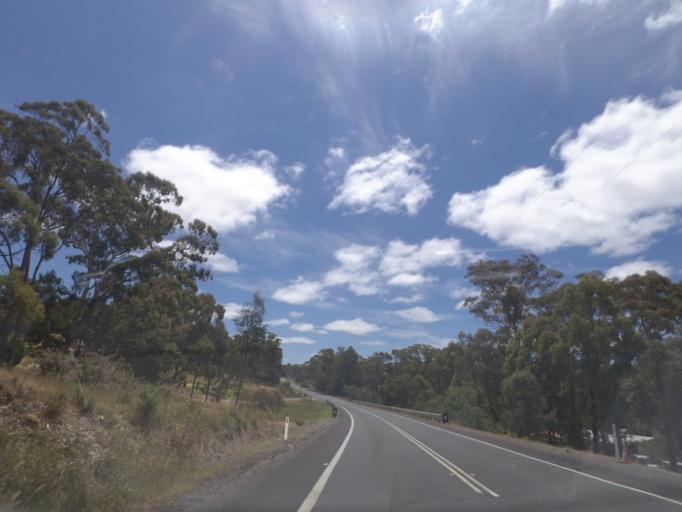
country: AU
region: Victoria
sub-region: Mount Alexander
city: Castlemaine
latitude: -37.2898
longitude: 144.1632
